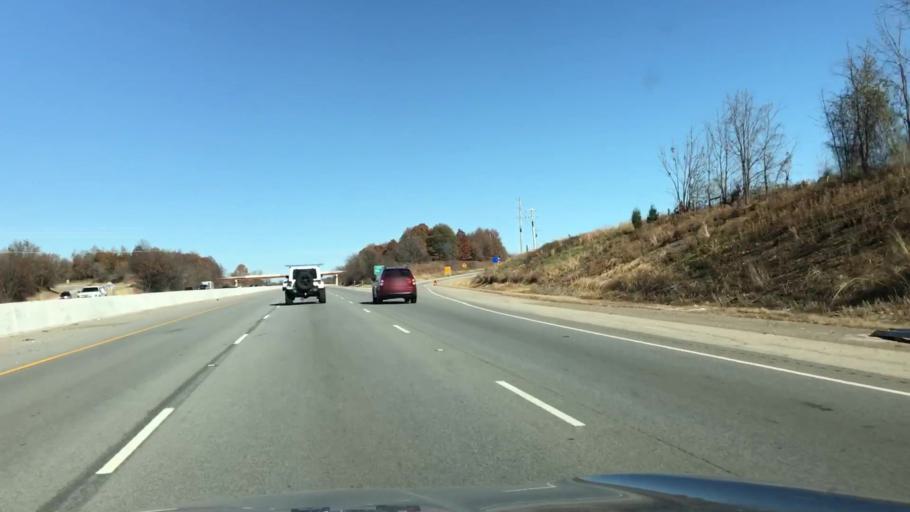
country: US
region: Arkansas
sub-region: Benton County
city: Bethel Heights
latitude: 36.2219
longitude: -94.1800
